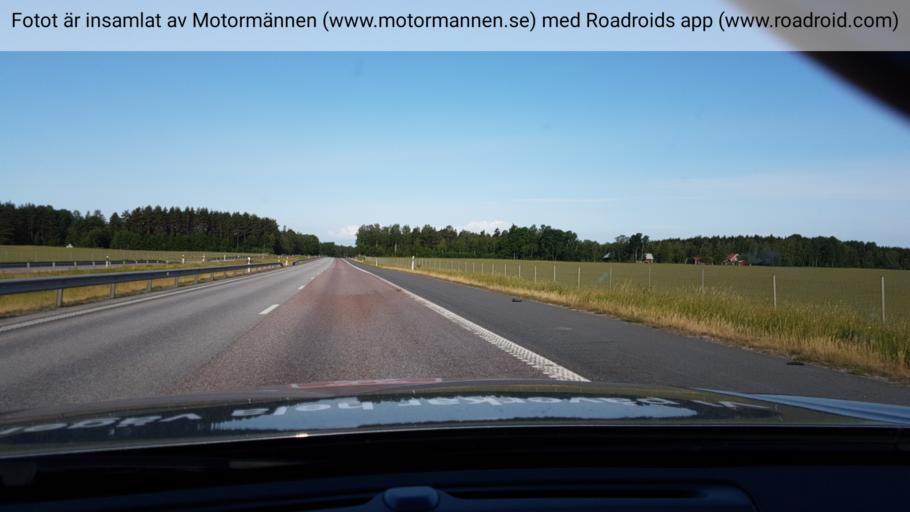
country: SE
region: OErebro
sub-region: Orebro Kommun
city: Hovsta
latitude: 59.3075
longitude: 15.3321
